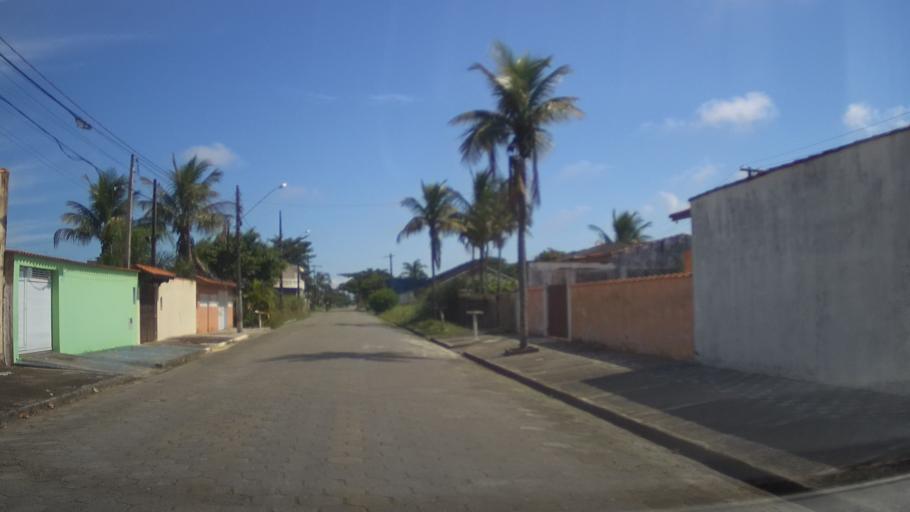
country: BR
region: Sao Paulo
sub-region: Itanhaem
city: Itanhaem
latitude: -24.1487
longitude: -46.7243
